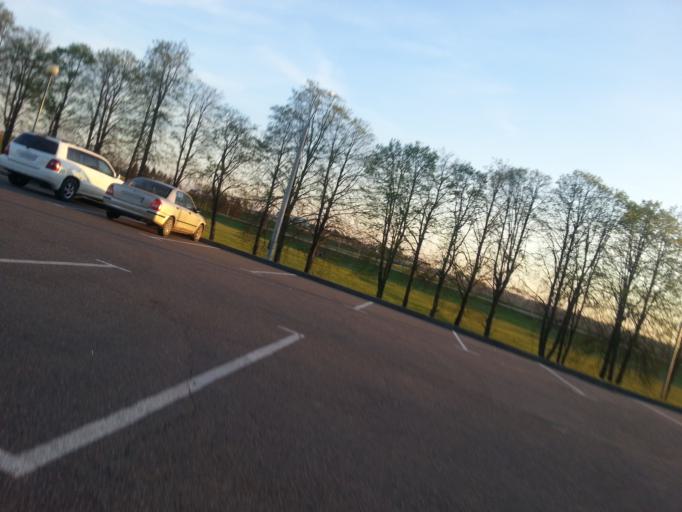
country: BY
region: Minsk
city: Slabada
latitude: 54.0191
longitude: 27.8920
